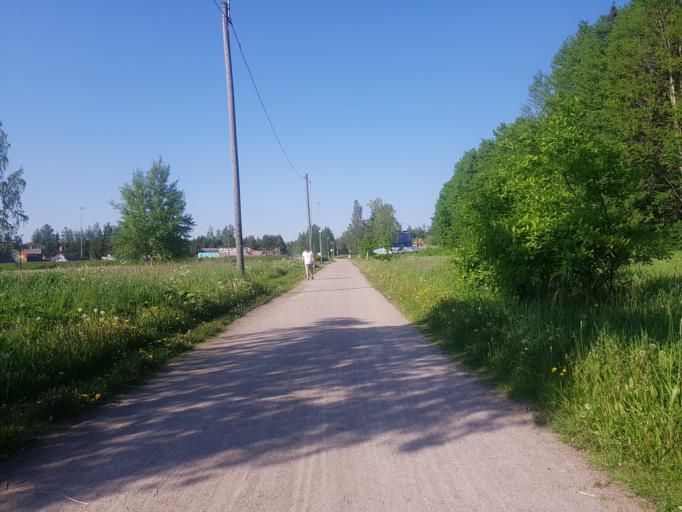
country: FI
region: Uusimaa
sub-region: Helsinki
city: Vantaa
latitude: 60.2343
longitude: 24.9955
